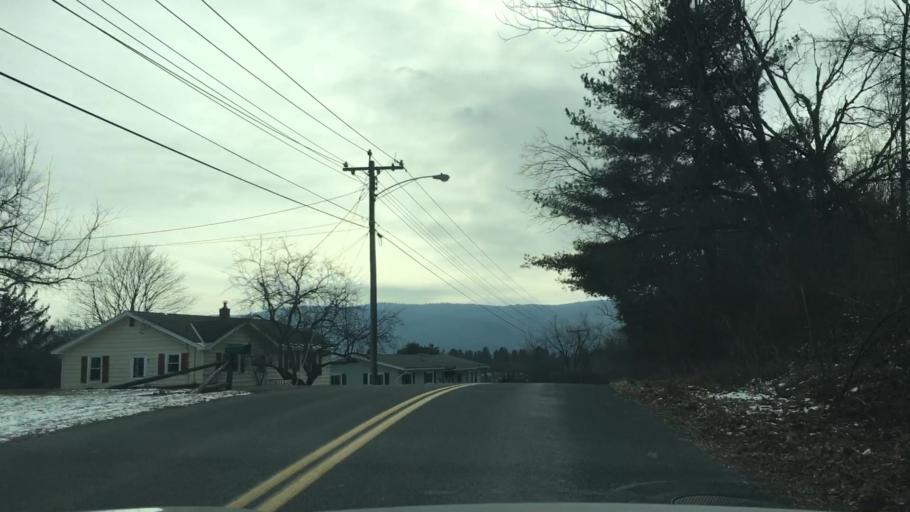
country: US
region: Massachusetts
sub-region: Berkshire County
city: Lee
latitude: 42.2889
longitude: -73.2449
